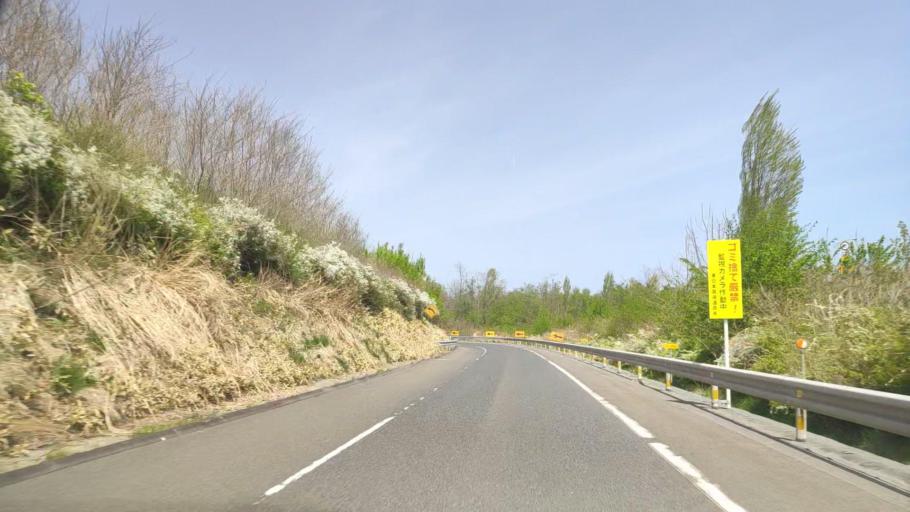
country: JP
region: Aomori
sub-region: Hachinohe Shi
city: Uchimaru
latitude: 40.4932
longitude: 141.4646
